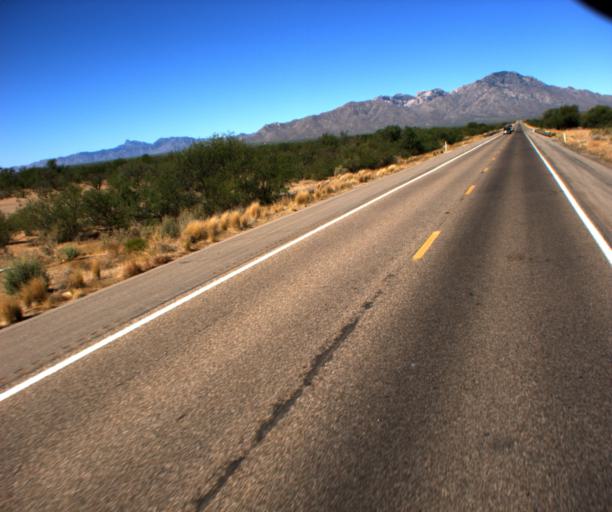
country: US
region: Arizona
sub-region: Pima County
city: Three Points
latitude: 32.0570
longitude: -111.4037
